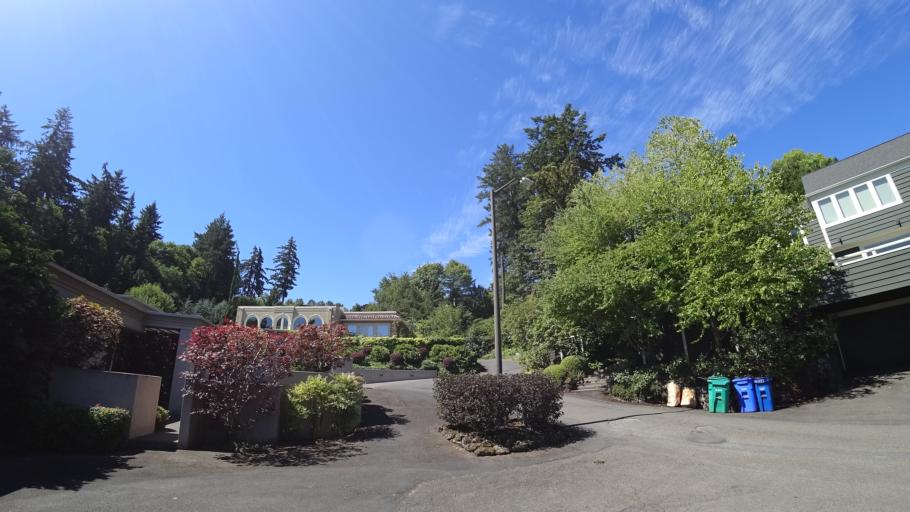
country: US
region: Oregon
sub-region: Multnomah County
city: Portland
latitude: 45.5091
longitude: -122.6935
